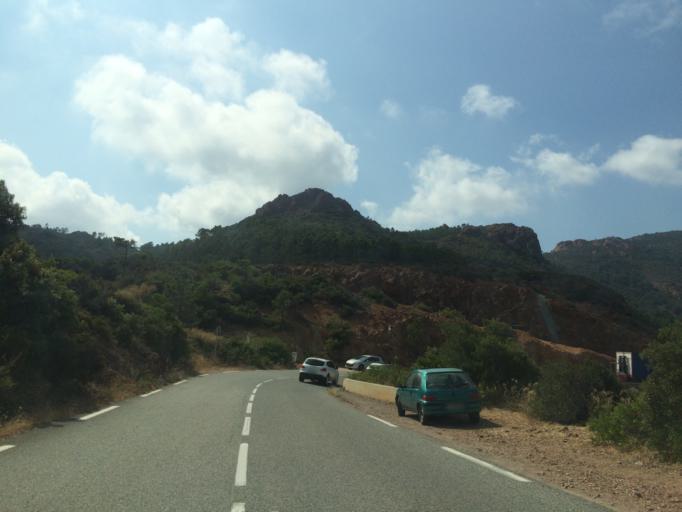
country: FR
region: Provence-Alpes-Cote d'Azur
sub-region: Departement des Alpes-Maritimes
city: Theoule-sur-Mer
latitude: 43.4412
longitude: 6.8987
